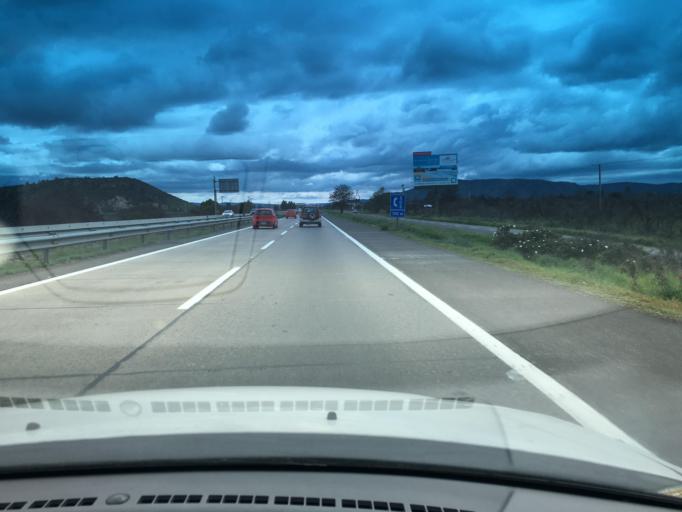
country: CL
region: Valparaiso
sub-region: Provincia de Marga Marga
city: Villa Alemana
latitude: -33.3610
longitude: -71.3205
